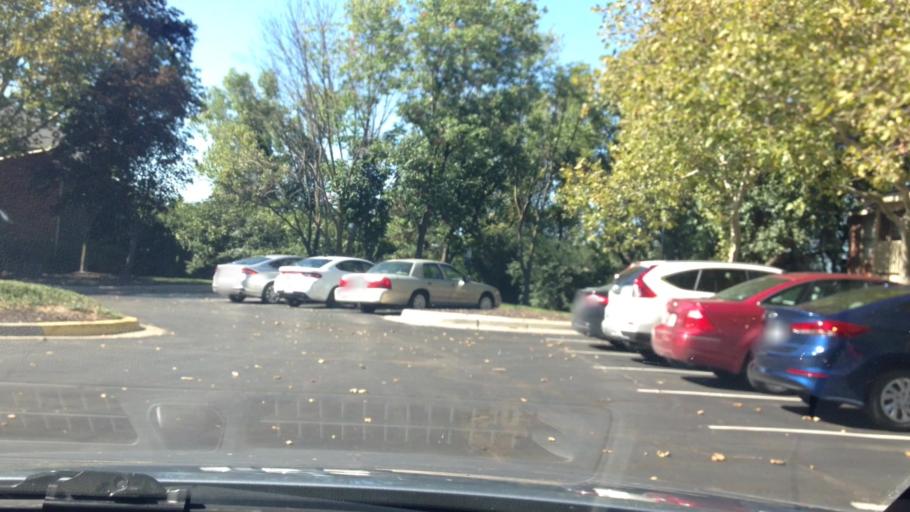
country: US
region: Kansas
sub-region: Johnson County
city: Roeland Park
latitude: 39.0474
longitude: -94.6421
